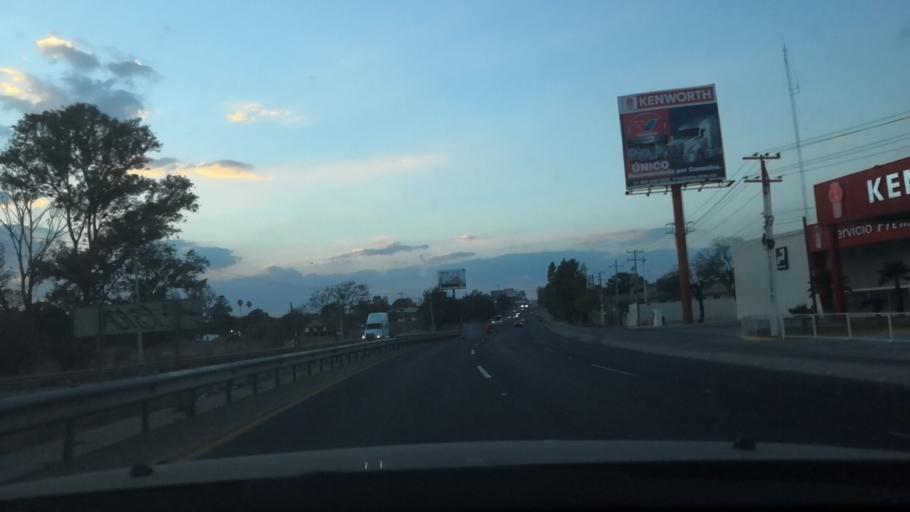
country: MX
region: Guanajuato
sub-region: Silao de la Victoria
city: El Refugio de los Sauces
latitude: 21.0268
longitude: -101.5417
